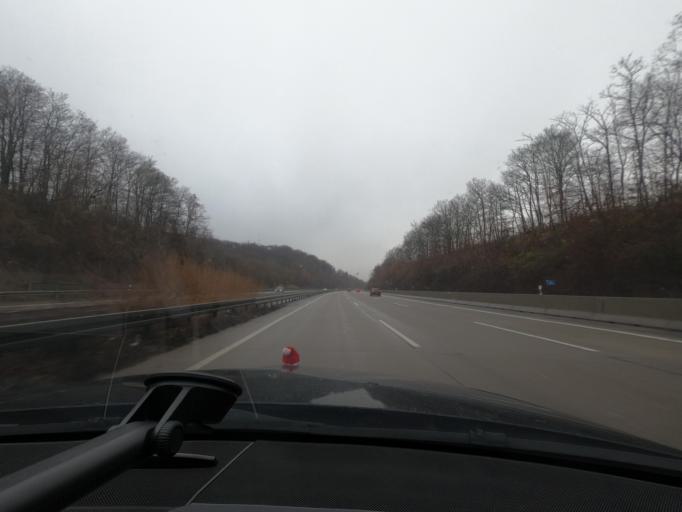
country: DE
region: Lower Saxony
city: Hildesheim
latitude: 52.1361
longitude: 10.0158
